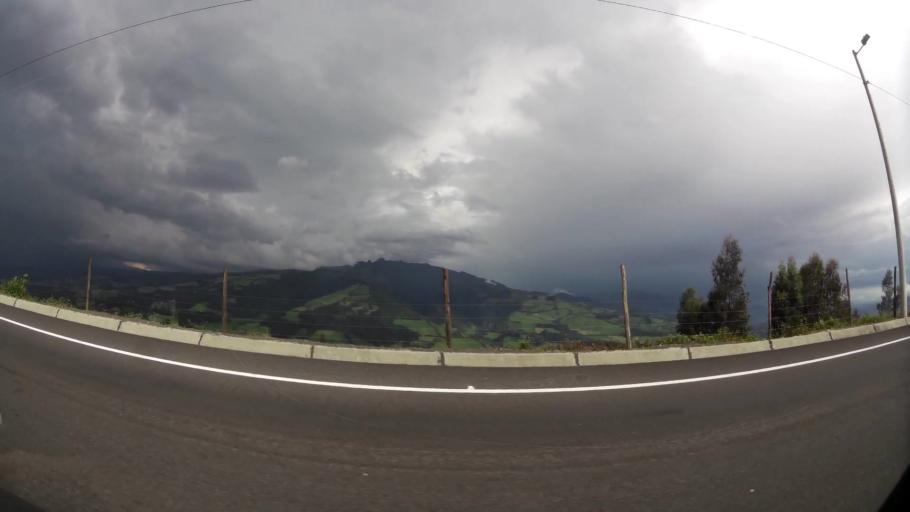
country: EC
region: Pichincha
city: Sangolqui
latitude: -0.3906
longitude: -78.5377
